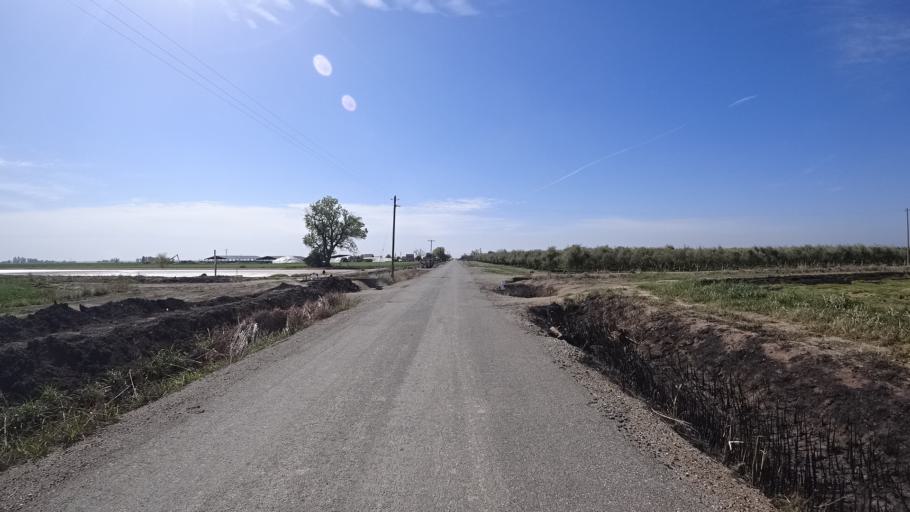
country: US
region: California
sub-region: Glenn County
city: Willows
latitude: 39.5948
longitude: -122.0885
